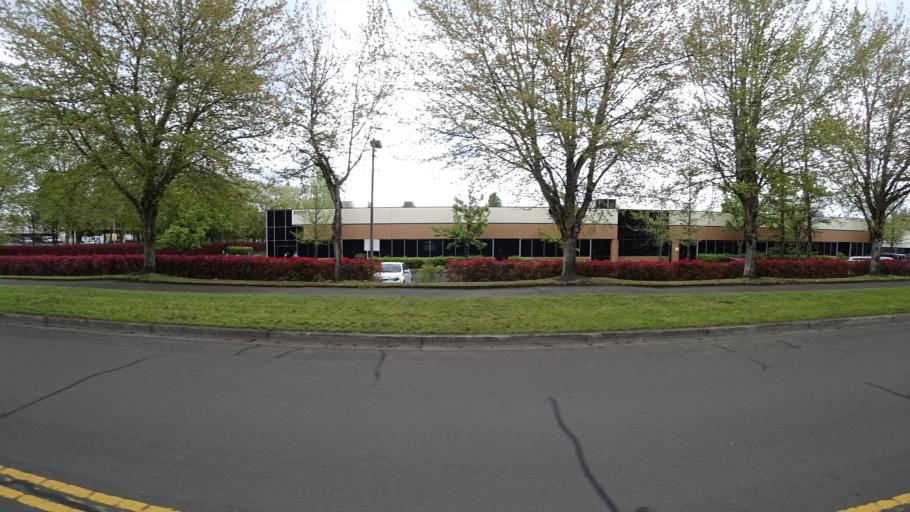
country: US
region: Oregon
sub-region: Washington County
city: Rockcreek
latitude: 45.5453
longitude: -122.8939
